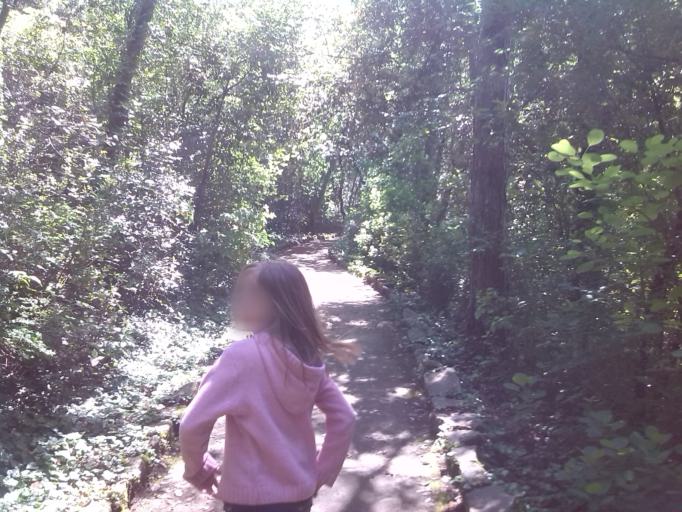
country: IT
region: Friuli Venezia Giulia
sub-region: Provincia di Trieste
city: Duino
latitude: 45.7733
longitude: 13.6083
